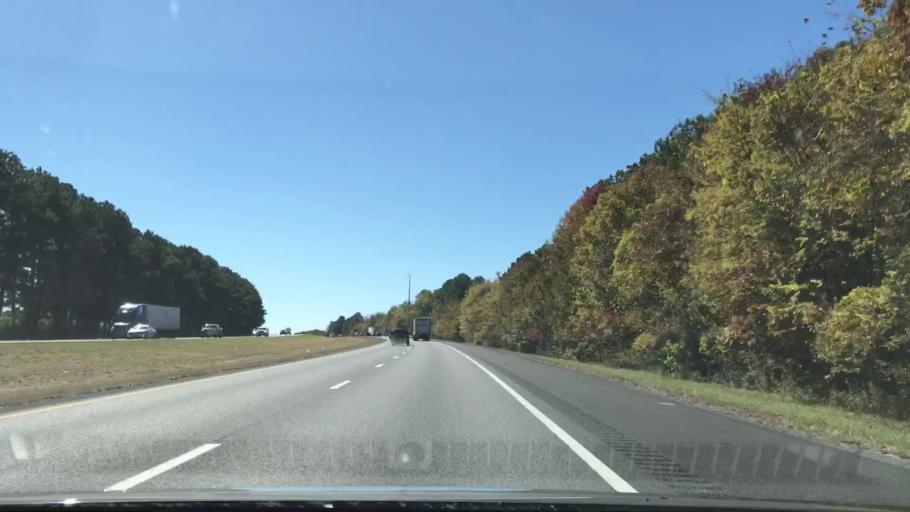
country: US
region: Tennessee
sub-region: Sumner County
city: White House
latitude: 36.4992
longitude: -86.6676
